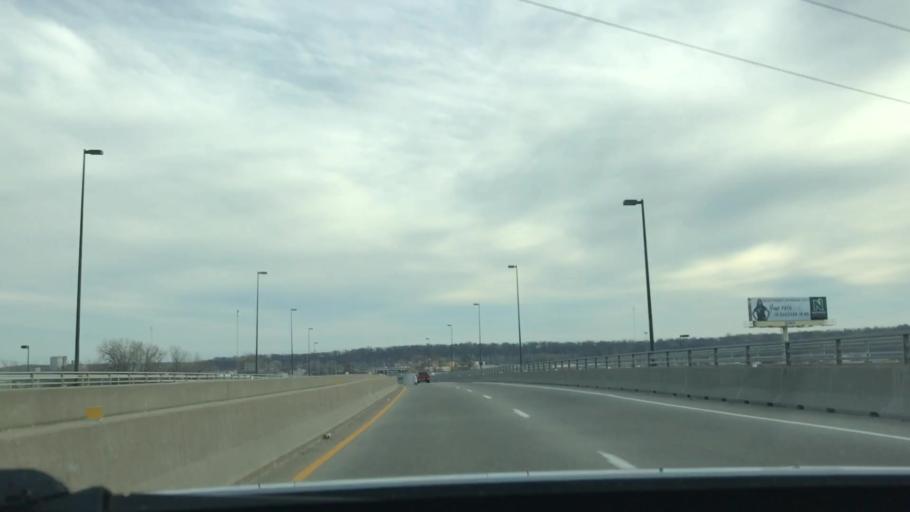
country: US
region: Missouri
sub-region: Clay County
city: North Kansas City
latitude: 39.1413
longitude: -94.5319
